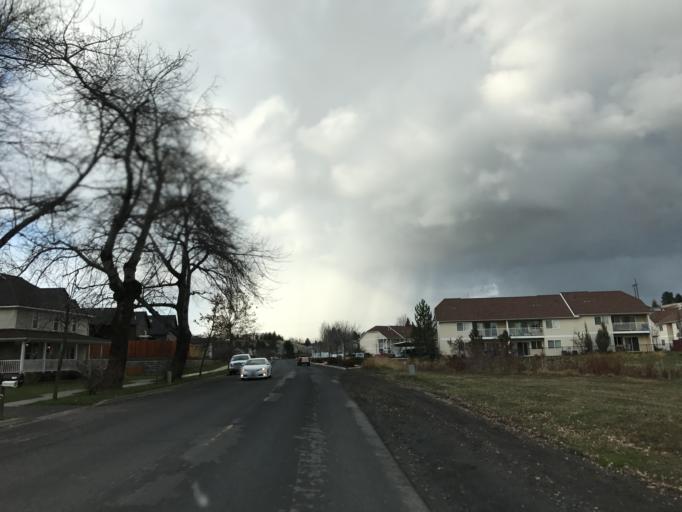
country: US
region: Idaho
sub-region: Latah County
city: Moscow
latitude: 46.7453
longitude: -116.9942
